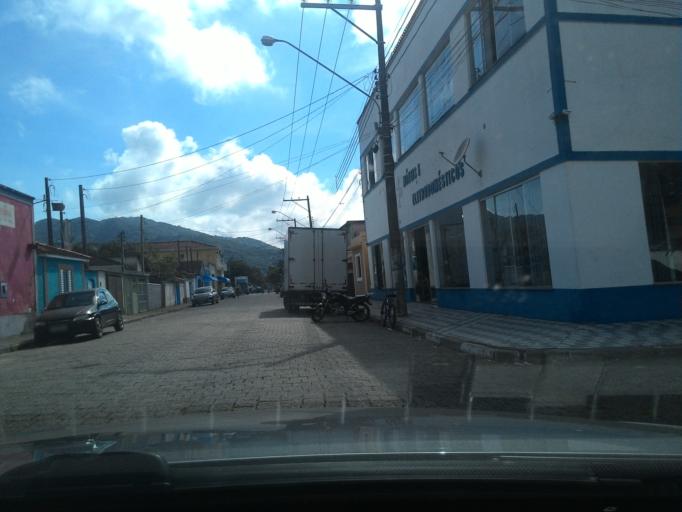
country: BR
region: Sao Paulo
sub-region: Iguape
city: Iguape
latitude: -24.7118
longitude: -47.5610
